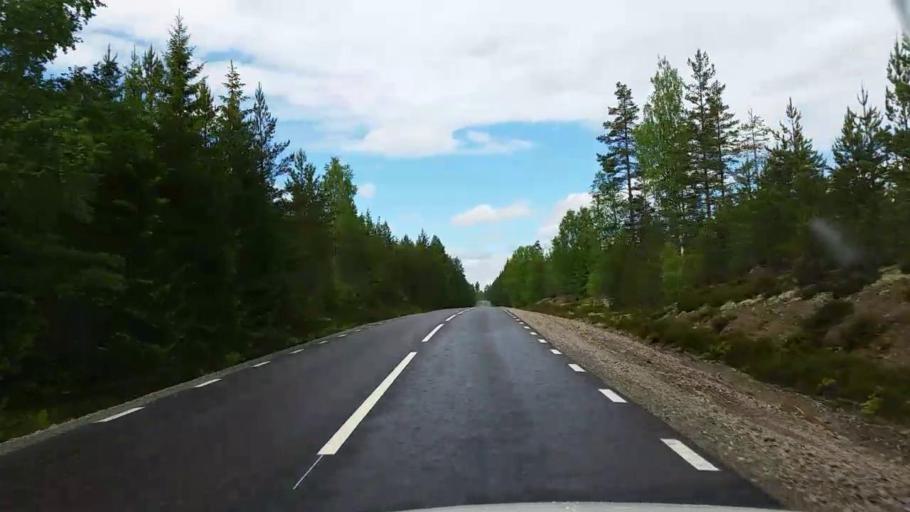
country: SE
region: Gaevleborg
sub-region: Sandvikens Kommun
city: Jarbo
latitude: 60.8708
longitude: 16.4084
